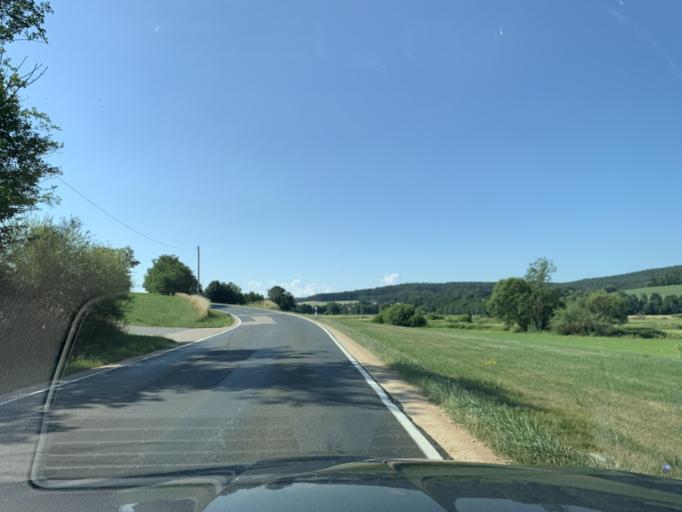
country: DE
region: Bavaria
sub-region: Upper Palatinate
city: Schwarzhofen
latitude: 49.3866
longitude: 12.3363
